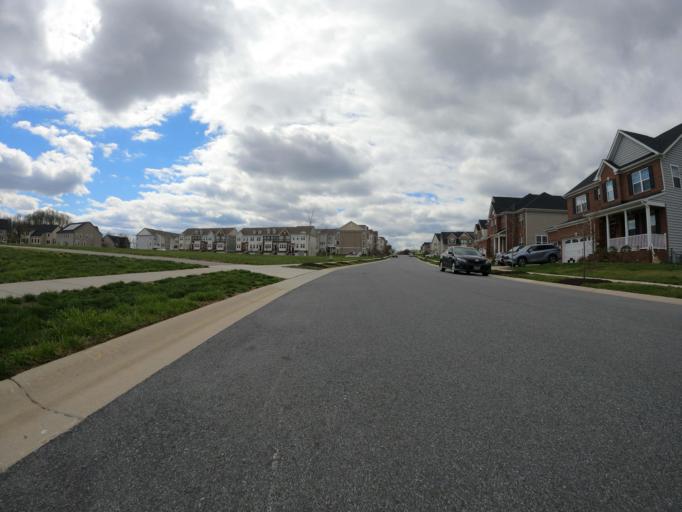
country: US
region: Maryland
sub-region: Howard County
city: North Laurel
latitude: 39.1473
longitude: -76.8486
